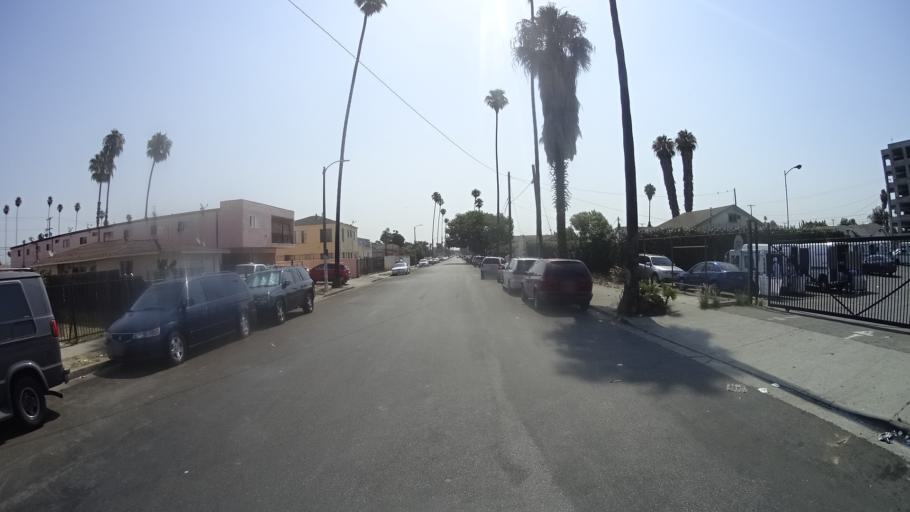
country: US
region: California
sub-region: Los Angeles County
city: Westmont
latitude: 33.9643
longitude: -118.2910
